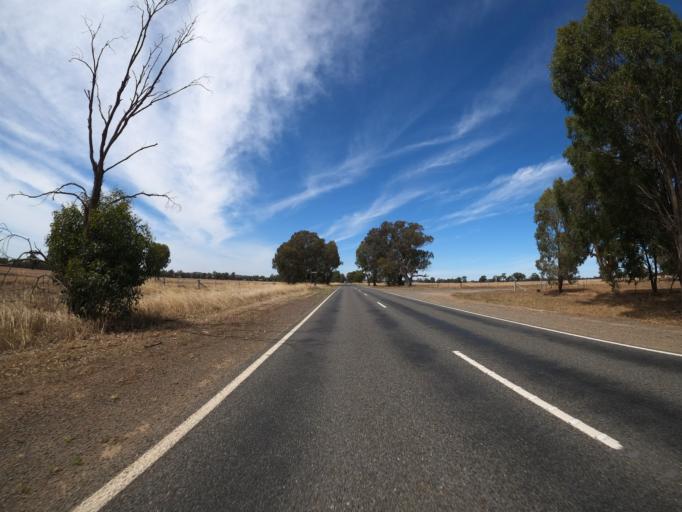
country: AU
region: Victoria
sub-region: Benalla
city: Benalla
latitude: -36.2841
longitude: 145.9523
